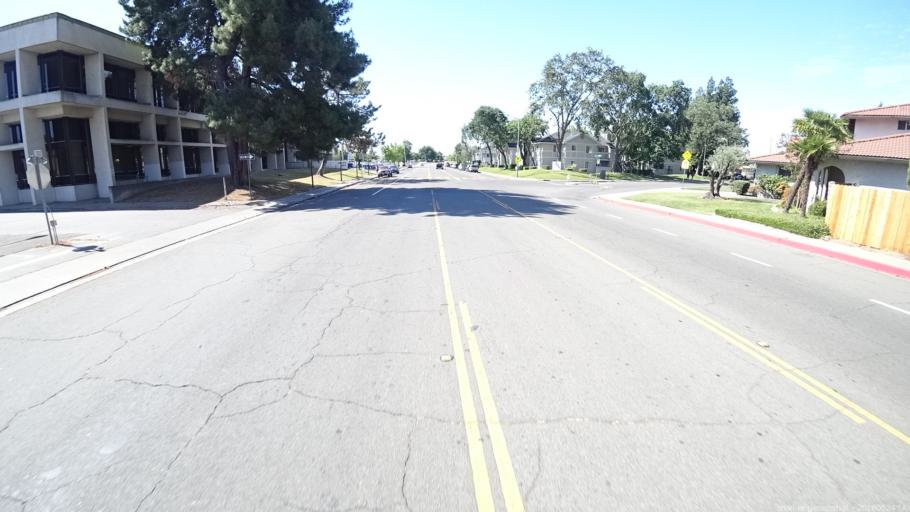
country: US
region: California
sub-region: Sacramento County
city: Sacramento
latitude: 38.6039
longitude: -121.4492
